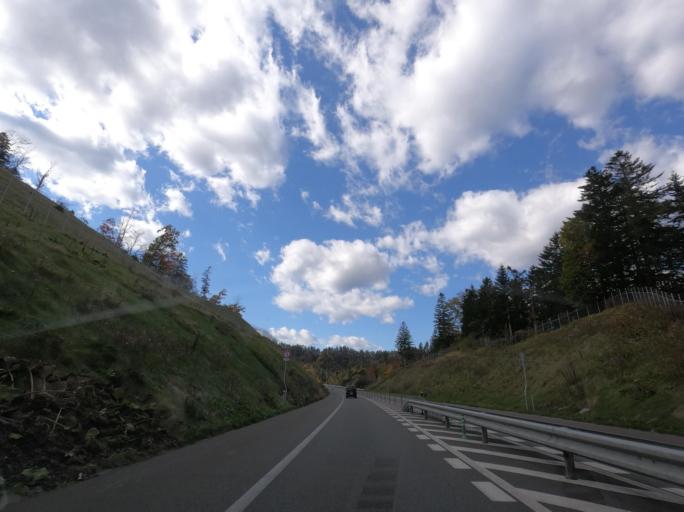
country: JP
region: Hokkaido
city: Kushiro
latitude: 43.0799
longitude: 144.0509
